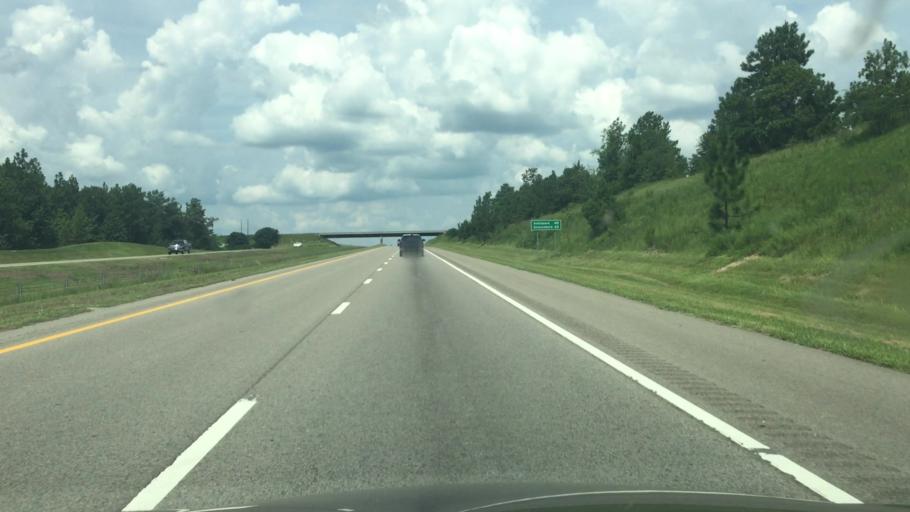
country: US
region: North Carolina
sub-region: Richmond County
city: Ellerbe
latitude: 35.1838
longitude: -79.7178
